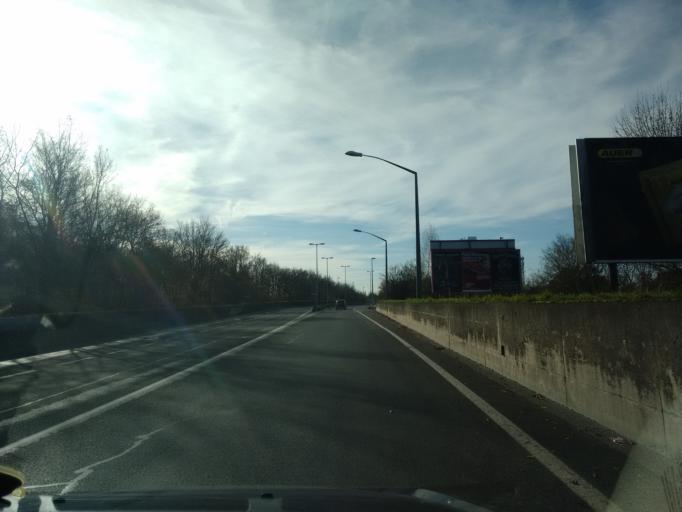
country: AT
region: Upper Austria
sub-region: Linz Stadt
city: Linz
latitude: 48.2621
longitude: 14.2998
